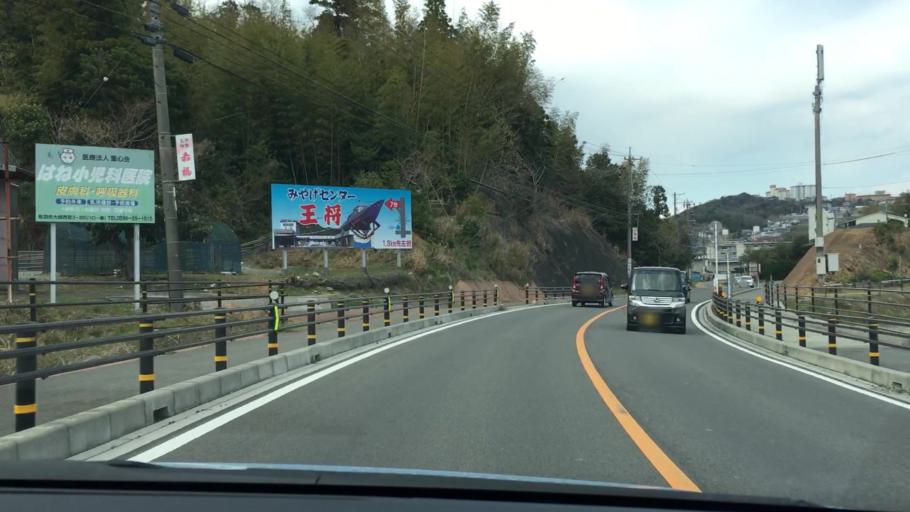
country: JP
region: Mie
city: Toba
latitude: 34.4639
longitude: 136.8549
